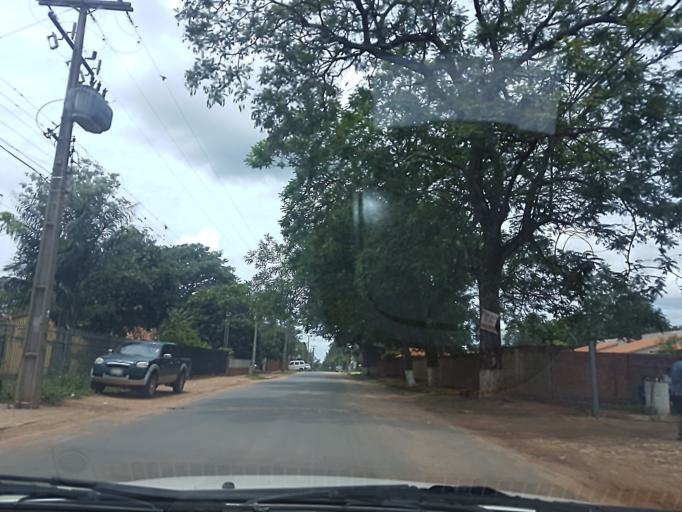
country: PY
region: Central
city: Colonia Mariano Roque Alonso
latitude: -25.1855
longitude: -57.5318
